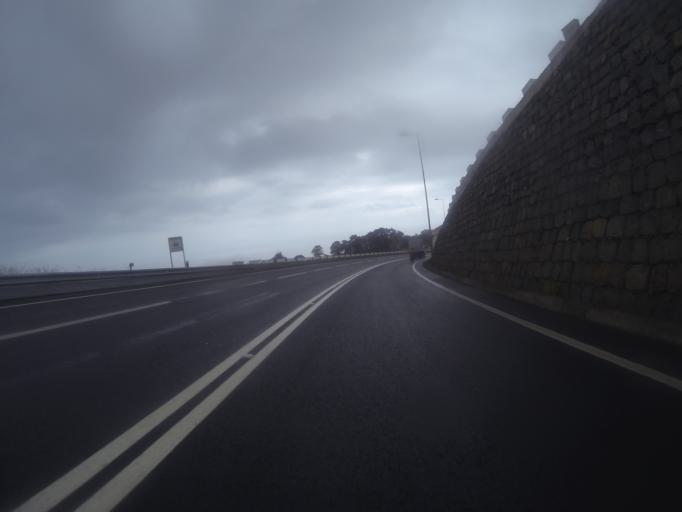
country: PT
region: Madeira
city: Canico
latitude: 32.6525
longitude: -16.8506
